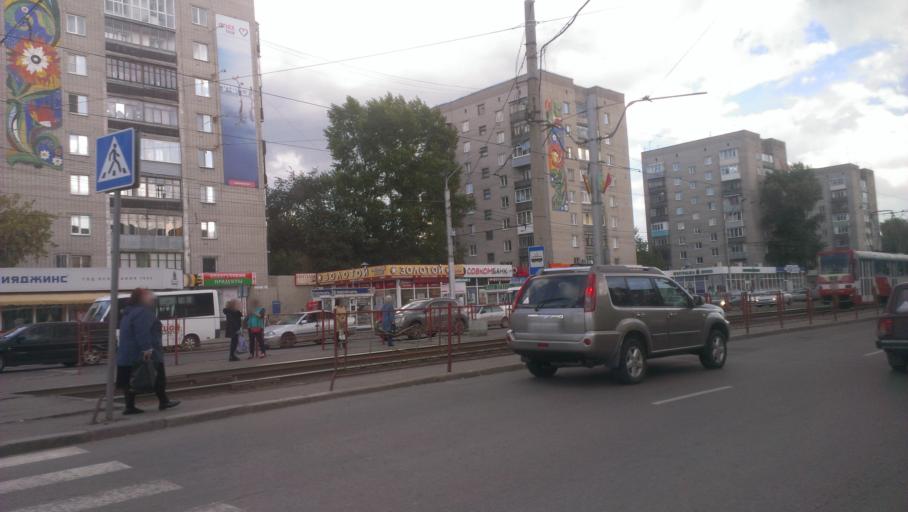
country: RU
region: Altai Krai
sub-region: Gorod Barnaulskiy
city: Barnaul
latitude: 53.3607
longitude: 83.7632
